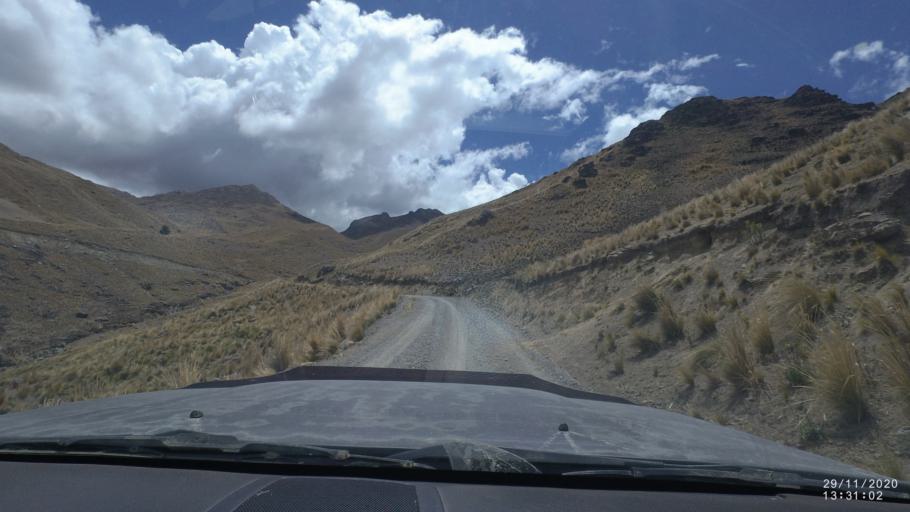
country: BO
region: Cochabamba
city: Cochabamba
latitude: -17.1037
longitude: -66.3421
